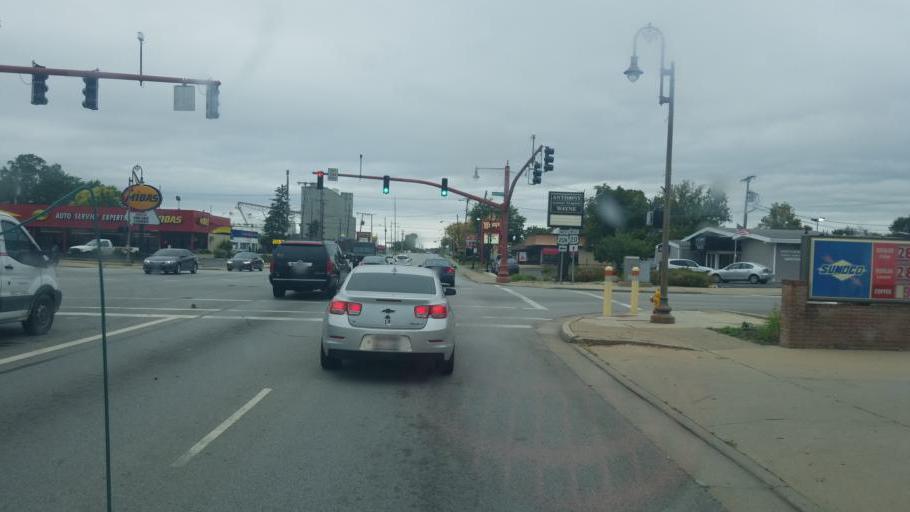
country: US
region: Ohio
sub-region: Lucas County
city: Maumee
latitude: 41.5668
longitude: -83.6559
